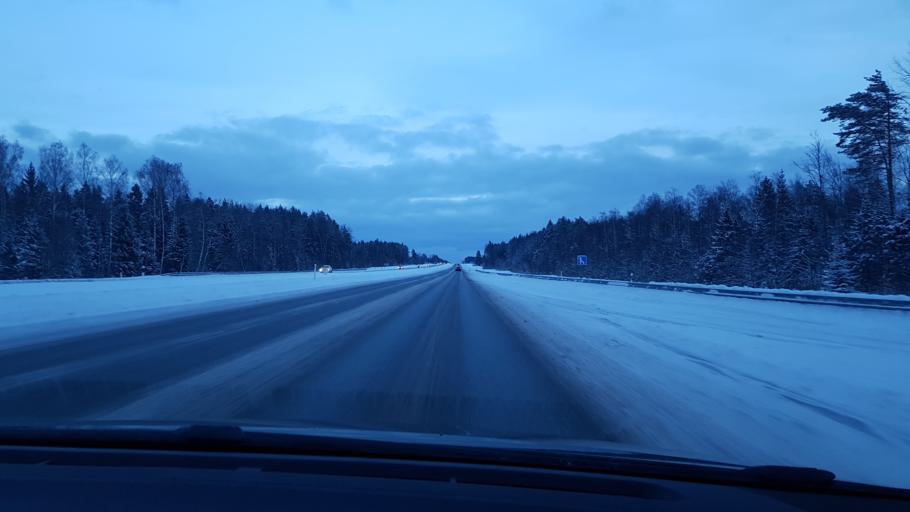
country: EE
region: Harju
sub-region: Raasiku vald
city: Raasiku
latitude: 59.4379
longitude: 25.2478
